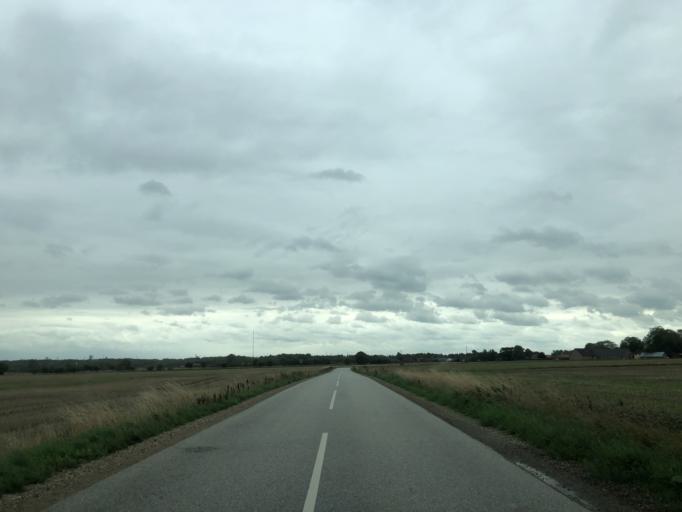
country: DK
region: Central Jutland
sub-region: Herning Kommune
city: Snejbjerg
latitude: 56.1426
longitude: 8.9030
